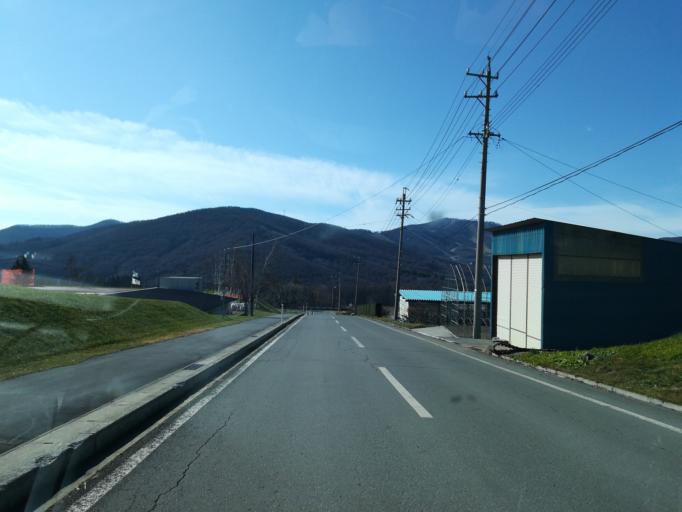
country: JP
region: Nagano
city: Suzaka
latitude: 36.5240
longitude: 138.3445
